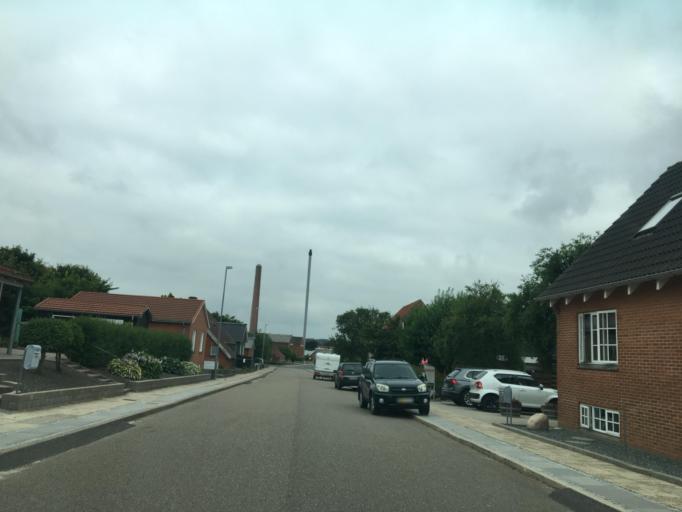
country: DK
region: North Denmark
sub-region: Thisted Kommune
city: Hurup
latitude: 56.7473
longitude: 8.4229
